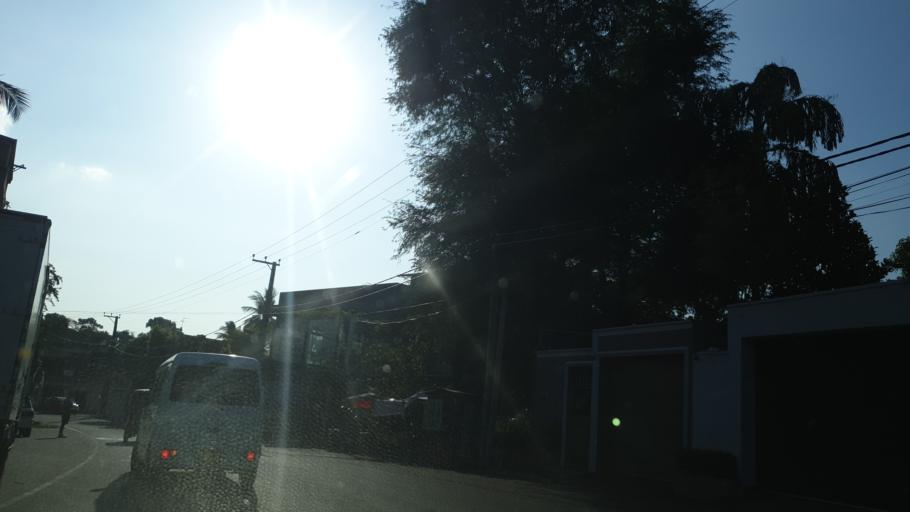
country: LK
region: Western
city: Galkissa
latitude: 6.8538
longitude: 79.8845
